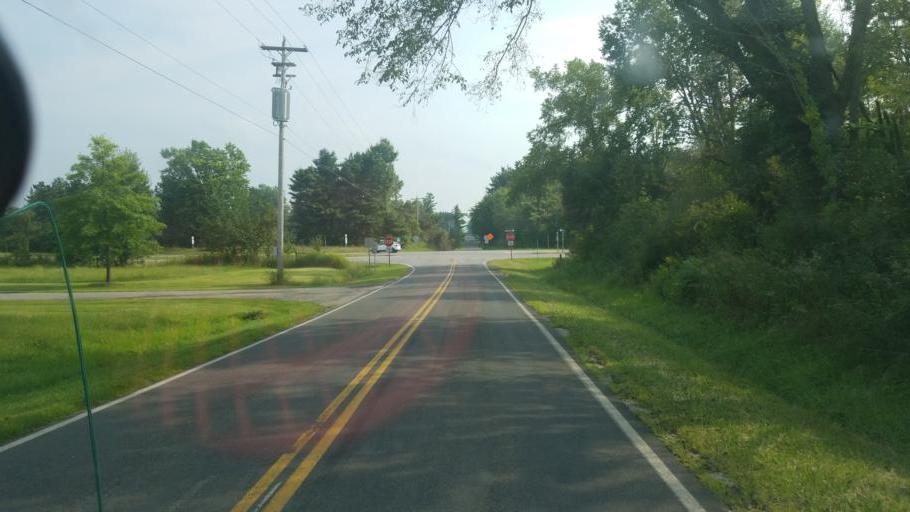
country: US
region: Ohio
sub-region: Medina County
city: Westfield Center
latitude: 41.0398
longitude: -81.9413
